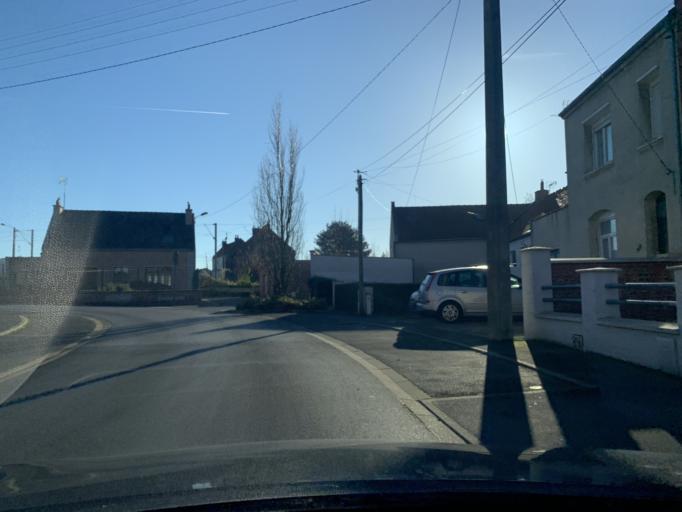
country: FR
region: Nord-Pas-de-Calais
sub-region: Departement du Nord
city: Cambrai
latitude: 50.1684
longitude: 3.2555
